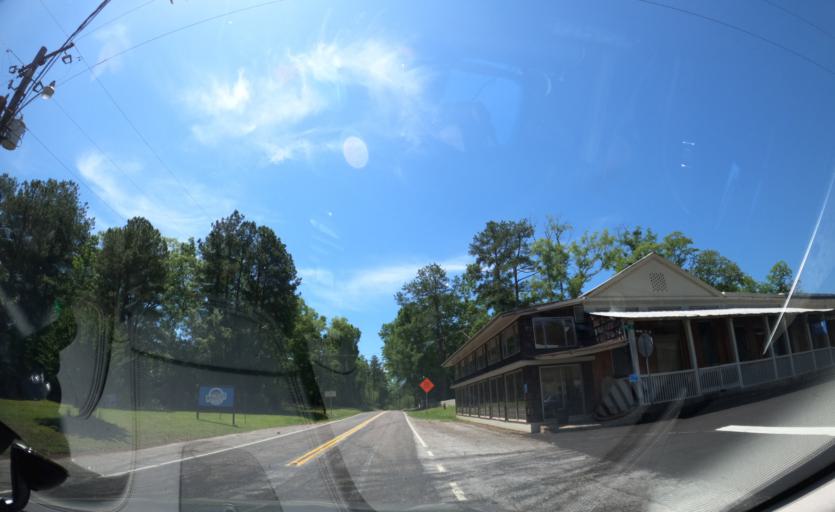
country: US
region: South Carolina
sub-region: Abbeville County
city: Calhoun Falls
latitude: 34.0073
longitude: -82.5072
